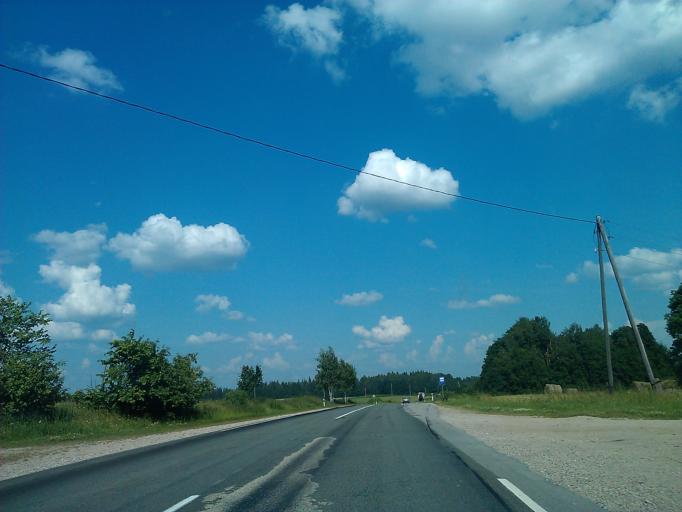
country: LV
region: Vainode
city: Vainode
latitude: 56.6157
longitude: 21.7938
